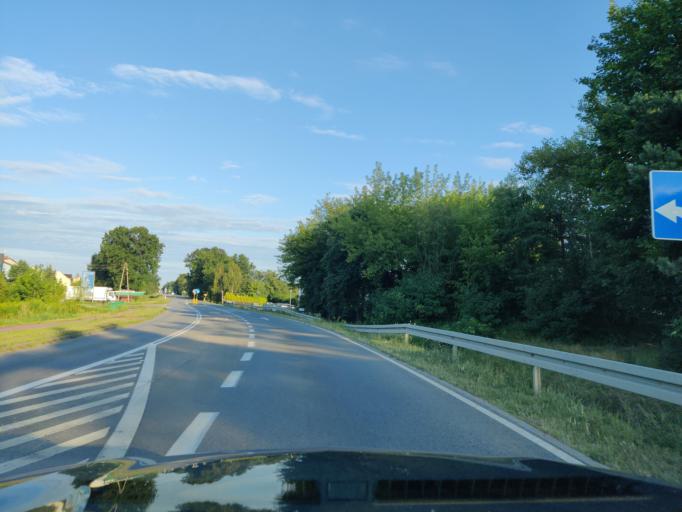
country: PL
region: Masovian Voivodeship
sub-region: Powiat pultuski
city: Pultusk
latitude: 52.6856
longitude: 21.1097
